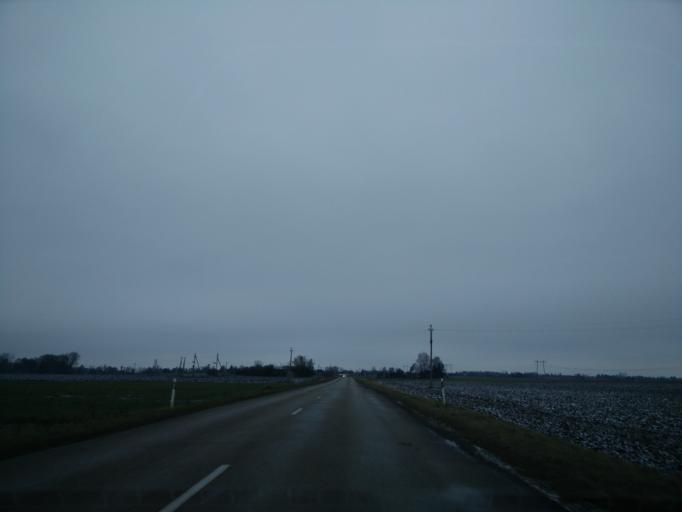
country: LT
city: Ariogala
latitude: 55.3178
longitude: 23.4302
